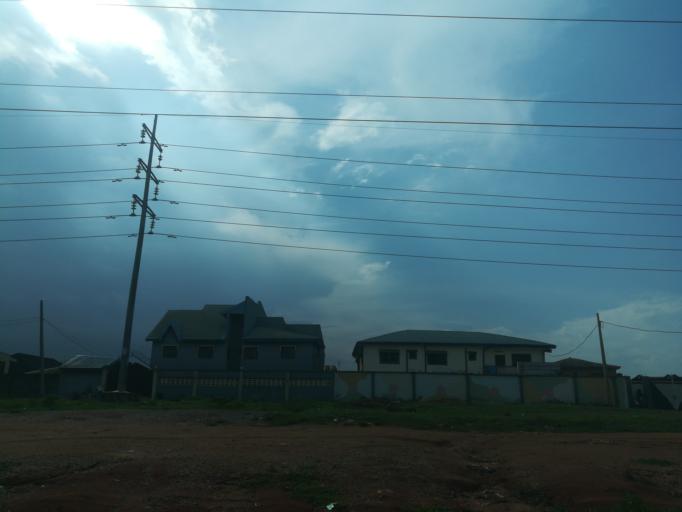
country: NG
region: Lagos
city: Ikorodu
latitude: 6.6302
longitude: 3.5108
